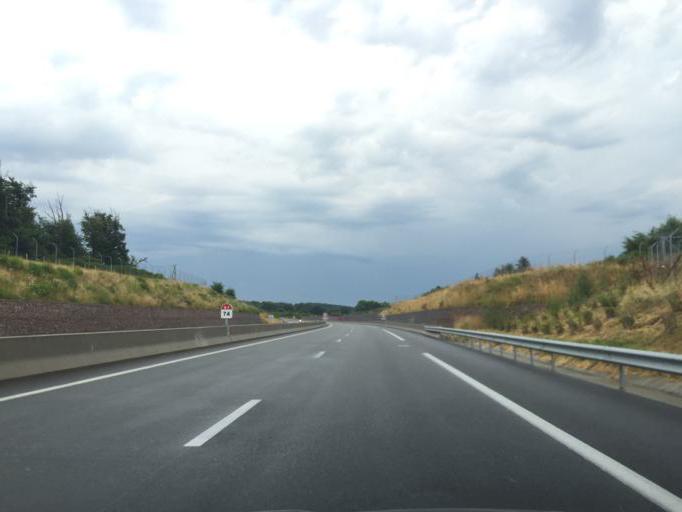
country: FR
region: Auvergne
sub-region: Departement de l'Allier
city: Lapalisse
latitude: 46.2166
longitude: 3.7088
